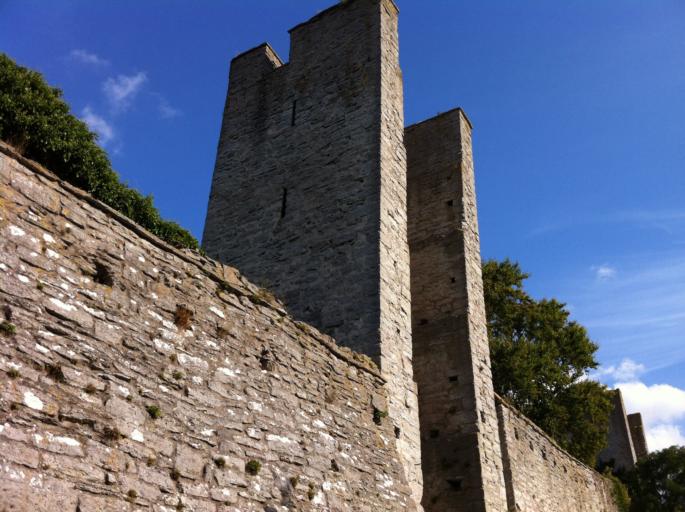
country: SE
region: Gotland
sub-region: Gotland
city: Visby
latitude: 57.6451
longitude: 18.3000
